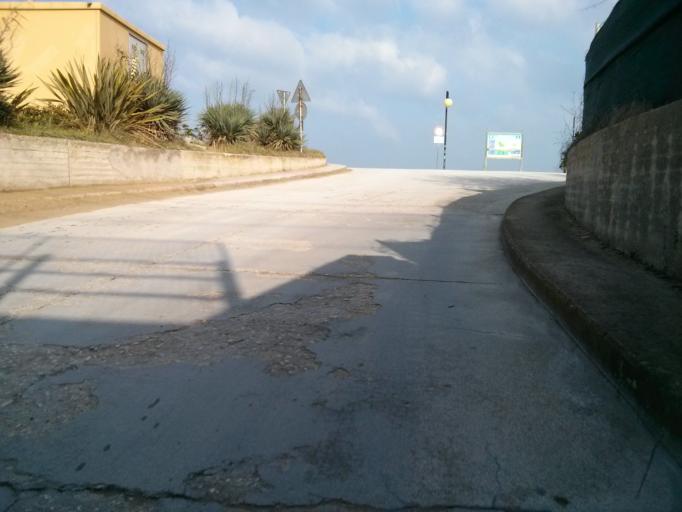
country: IT
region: The Marches
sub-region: Provincia di Pesaro e Urbino
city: Fenile
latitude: 43.8810
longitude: 12.9621
